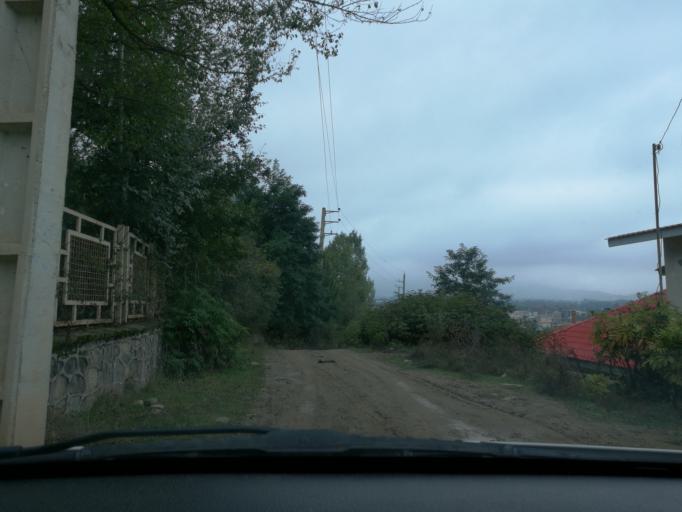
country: IR
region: Mazandaran
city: `Abbasabad
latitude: 36.5019
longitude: 51.2080
